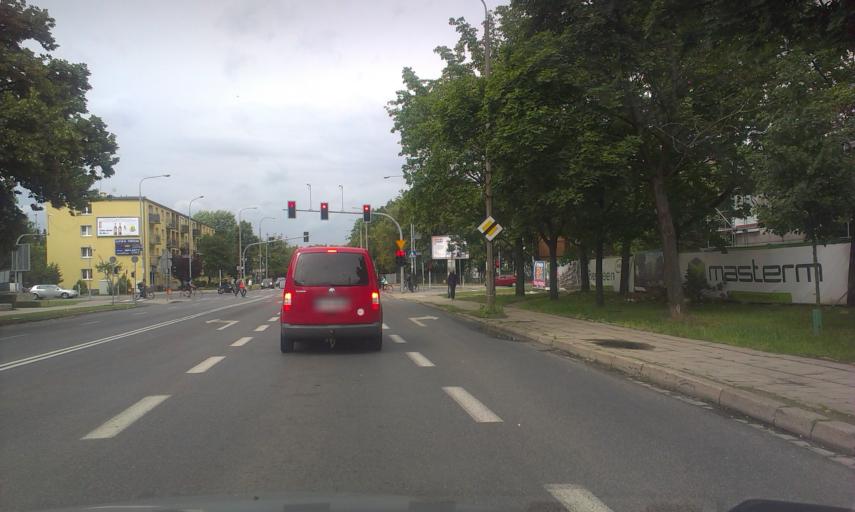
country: PL
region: Greater Poland Voivodeship
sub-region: Poznan
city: Poznan
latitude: 52.4106
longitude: 16.8767
